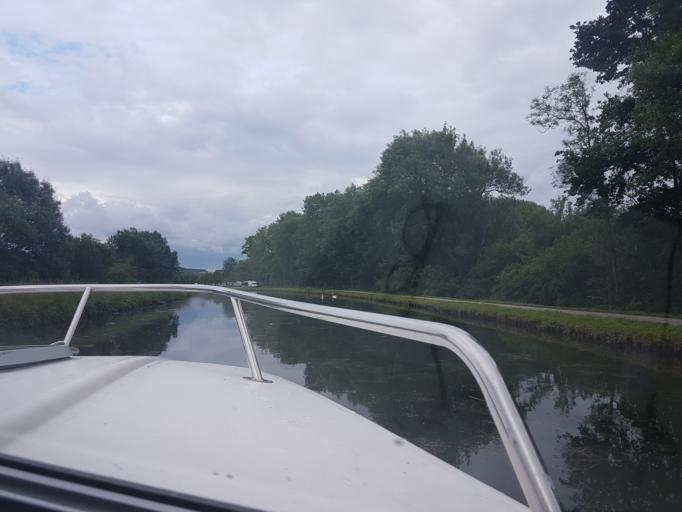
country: FR
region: Bourgogne
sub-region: Departement de l'Yonne
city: Saint-Bris-le-Vineux
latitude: 47.6967
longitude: 3.6440
